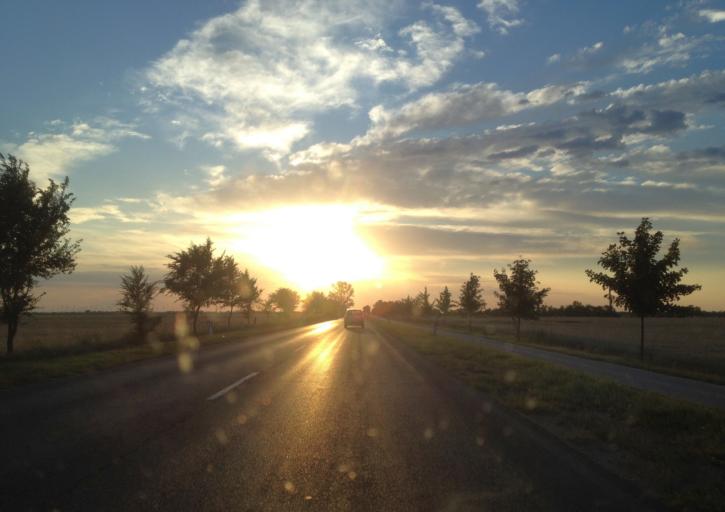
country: HU
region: Gyor-Moson-Sopron
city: Mosonmagyarovar
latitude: 47.8868
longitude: 17.2357
